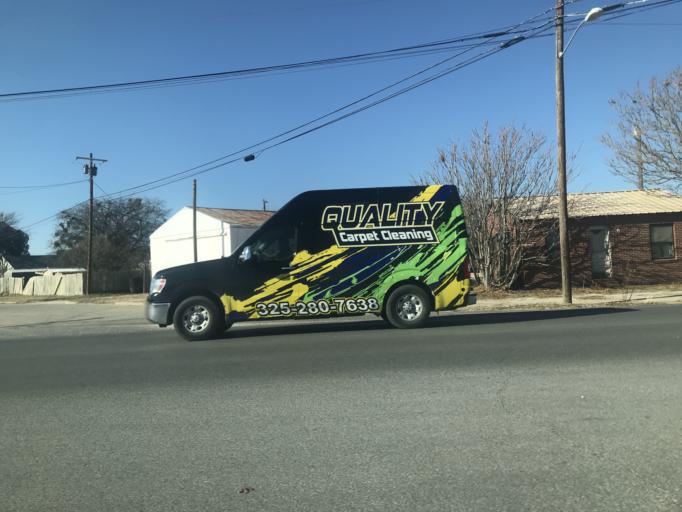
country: US
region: Texas
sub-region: Taylor County
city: Abilene
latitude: 32.4191
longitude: -99.7400
